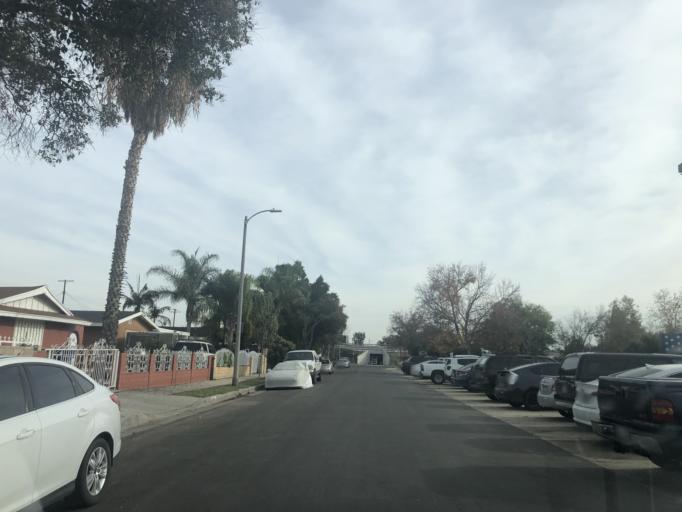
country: US
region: California
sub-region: Los Angeles County
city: San Fernando
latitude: 34.2695
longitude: -118.4376
